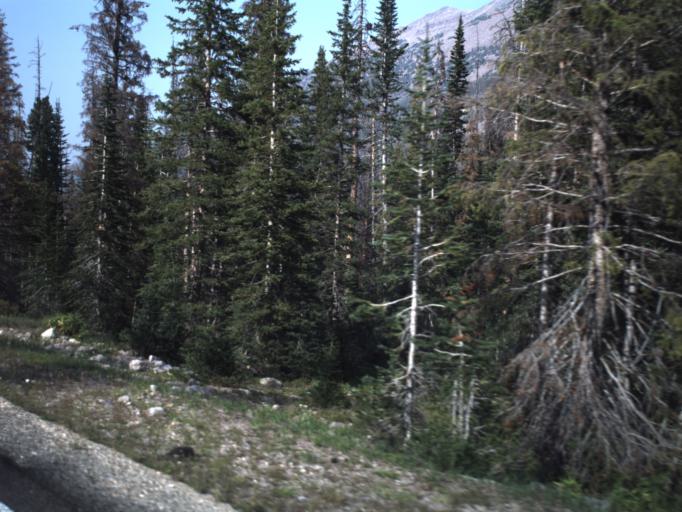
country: US
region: Utah
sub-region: Summit County
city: Kamas
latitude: 40.7433
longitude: -110.8718
